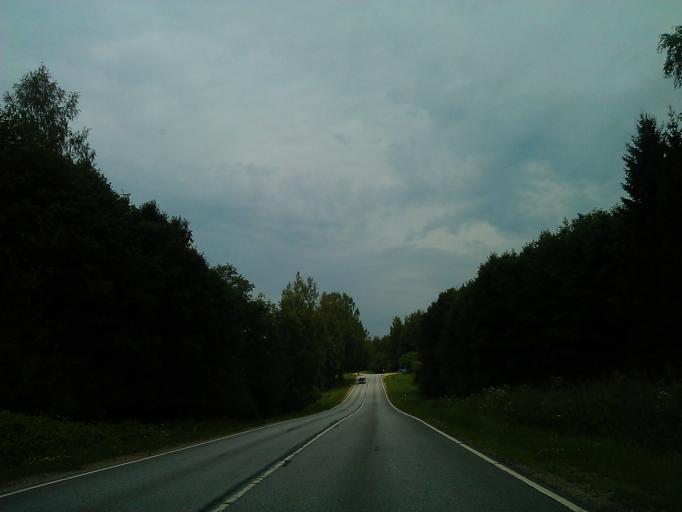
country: LV
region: Beverina
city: Murmuiza
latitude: 57.4454
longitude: 25.4319
